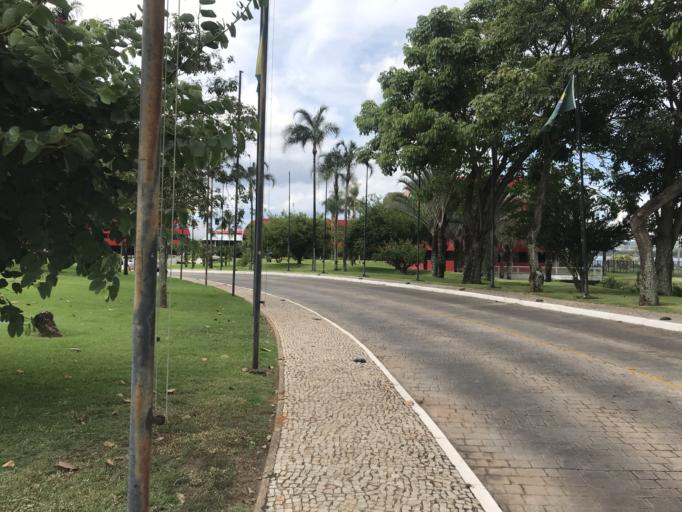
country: BR
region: Federal District
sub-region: Brasilia
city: Brasilia
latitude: -15.7902
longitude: -47.8288
